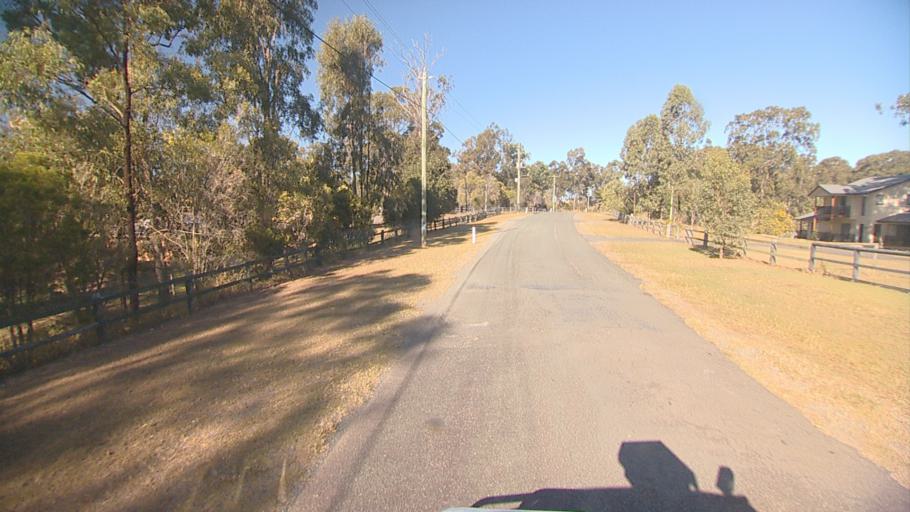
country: AU
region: Queensland
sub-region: Ipswich
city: Springfield Lakes
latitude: -27.7011
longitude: 152.9297
